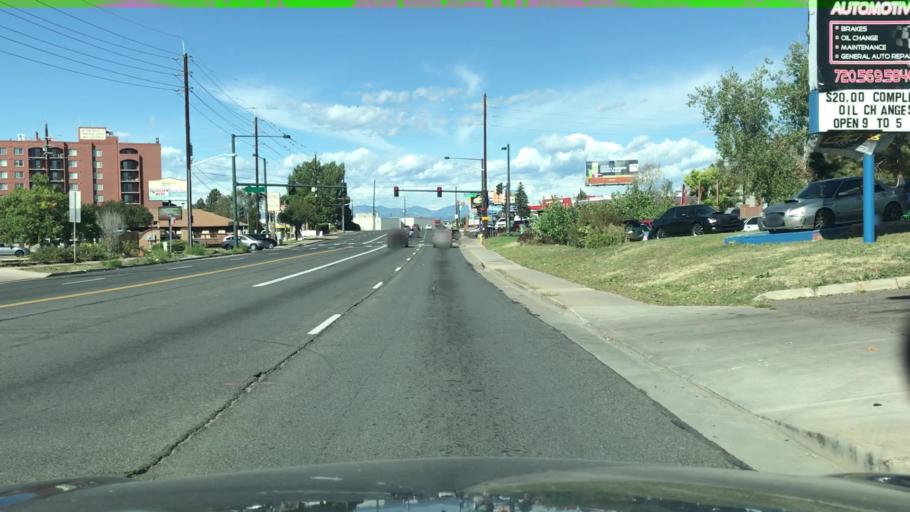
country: US
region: Colorado
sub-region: Arapahoe County
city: Glendale
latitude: 39.6999
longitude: -104.9071
